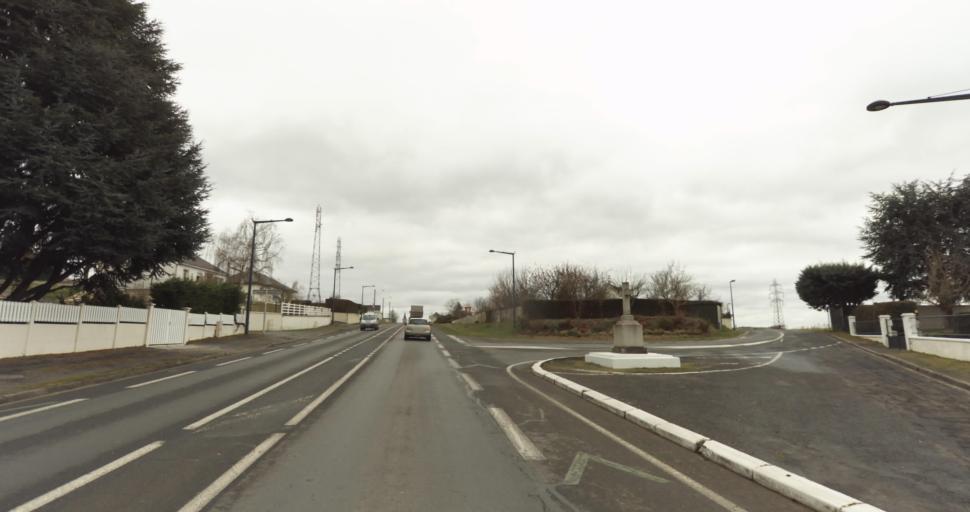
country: FR
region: Pays de la Loire
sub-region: Departement de Maine-et-Loire
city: Varrains
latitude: 47.2319
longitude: -0.0728
